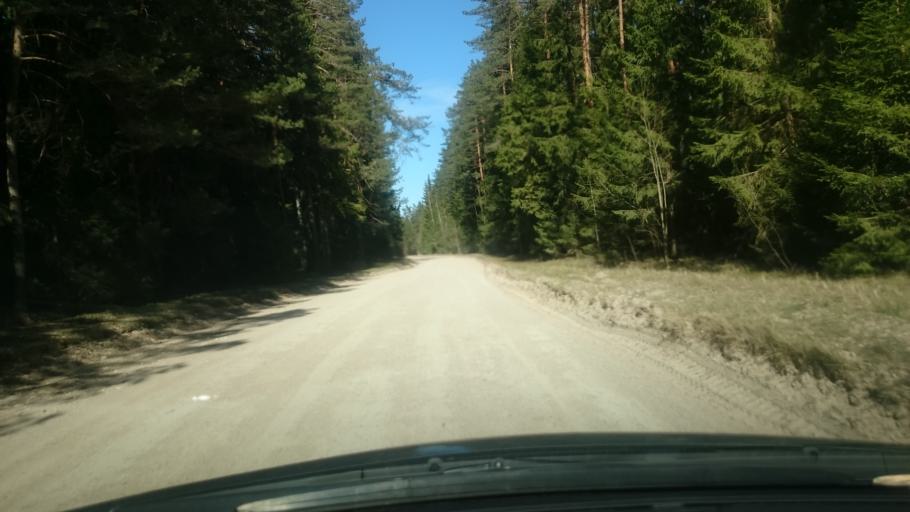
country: EE
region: Polvamaa
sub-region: Polva linn
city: Polva
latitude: 58.1528
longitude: 27.0509
